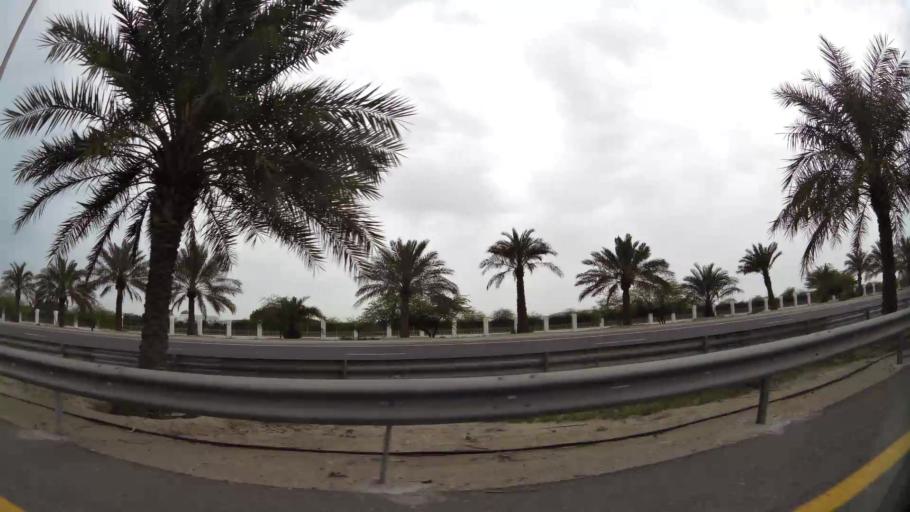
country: BH
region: Central Governorate
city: Dar Kulayb
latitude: 26.0625
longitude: 50.5216
